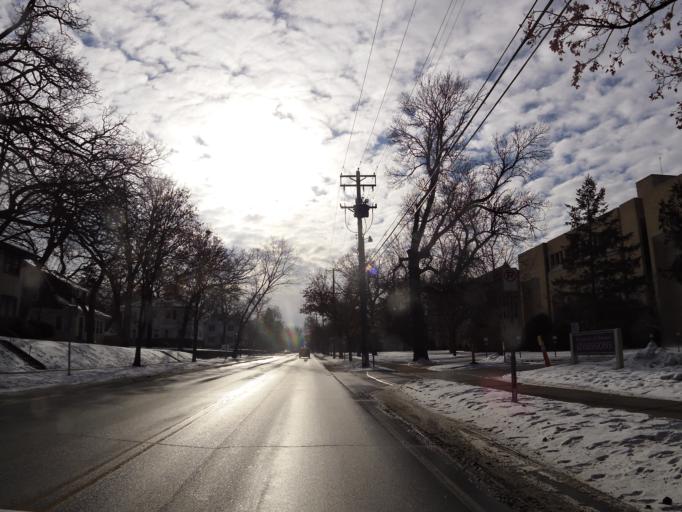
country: US
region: Minnesota
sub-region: Ramsey County
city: Falcon Heights
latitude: 44.9439
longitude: -93.1875
